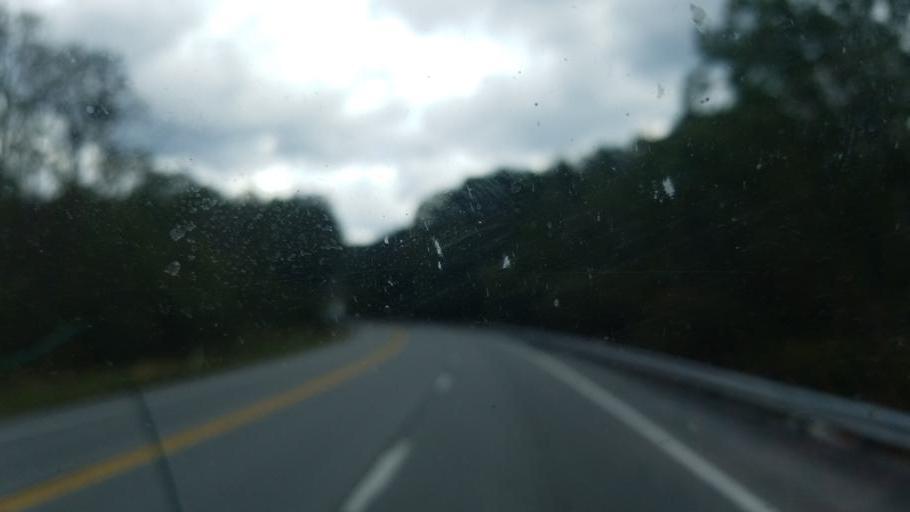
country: US
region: Pennsylvania
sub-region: Fulton County
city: McConnellsburg
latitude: 39.9464
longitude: -77.9748
